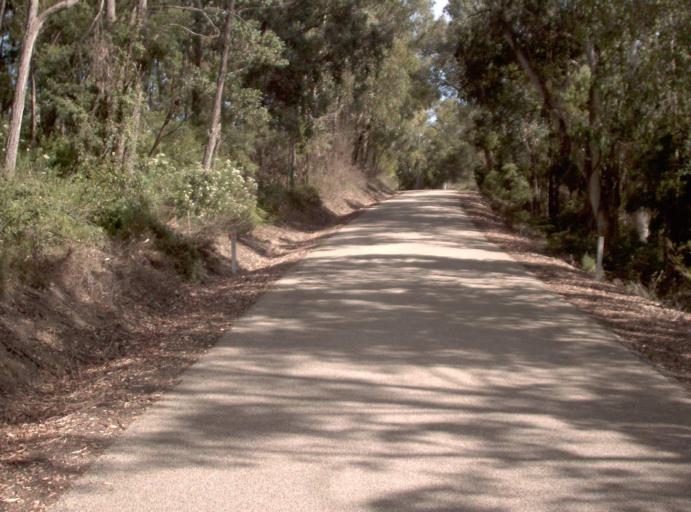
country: AU
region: Victoria
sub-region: East Gippsland
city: Lakes Entrance
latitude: -37.5232
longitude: 148.1403
